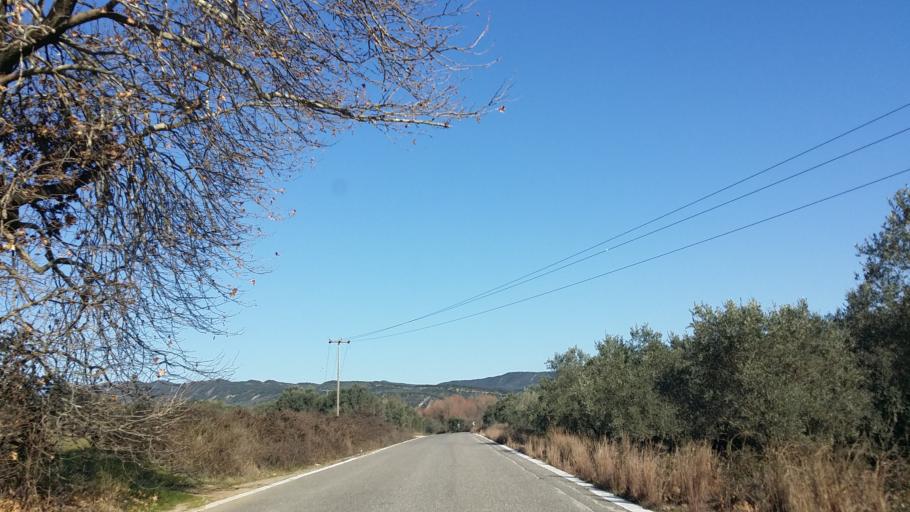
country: GR
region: West Greece
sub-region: Nomos Aitolias kai Akarnanias
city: Lepenou
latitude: 38.7266
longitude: 21.3339
